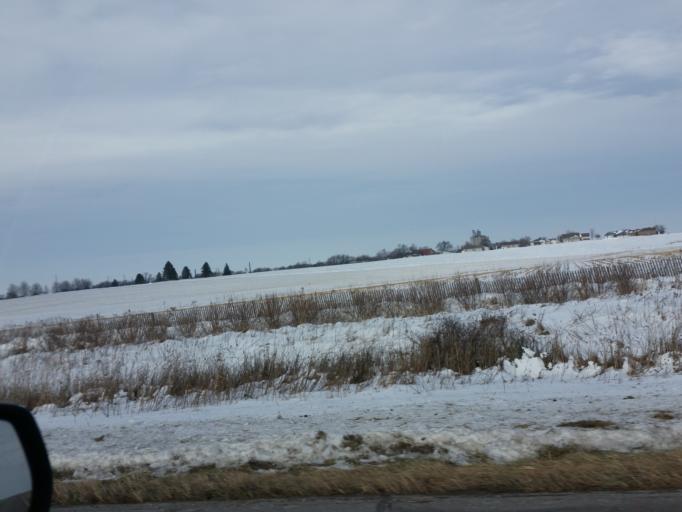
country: US
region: Iowa
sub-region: Buchanan County
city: Independence
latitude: 42.4616
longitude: -91.7295
